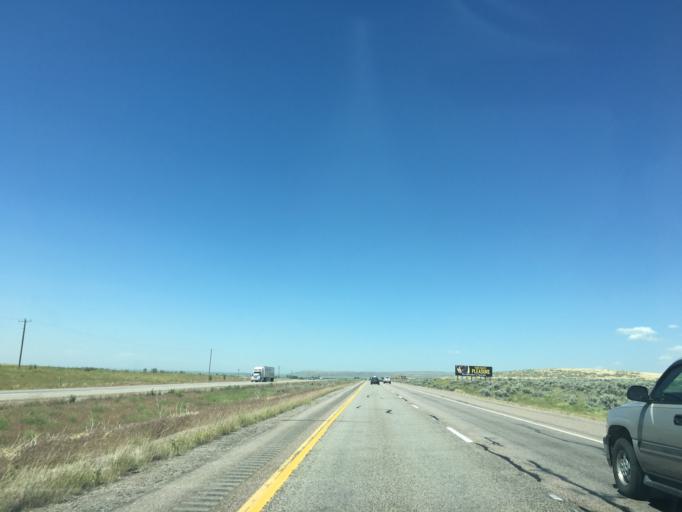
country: US
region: Idaho
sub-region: Bingham County
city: Fort Hall
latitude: 42.9850
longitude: -112.4186
